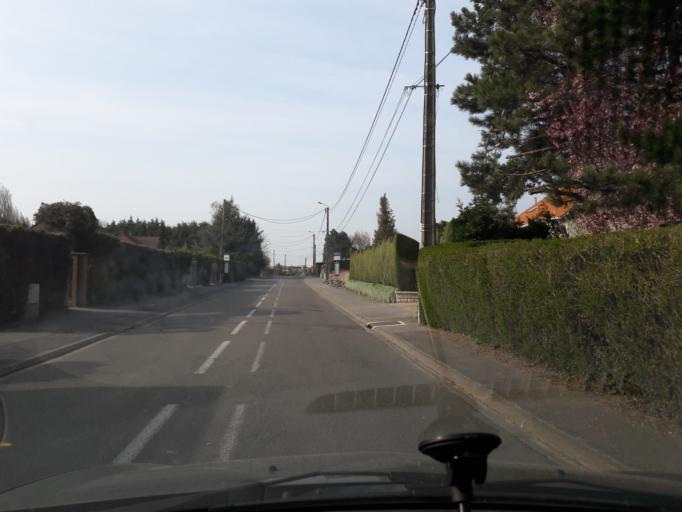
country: FR
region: Nord-Pas-de-Calais
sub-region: Departement du Nord
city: Rousies
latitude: 50.2605
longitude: 4.0094
